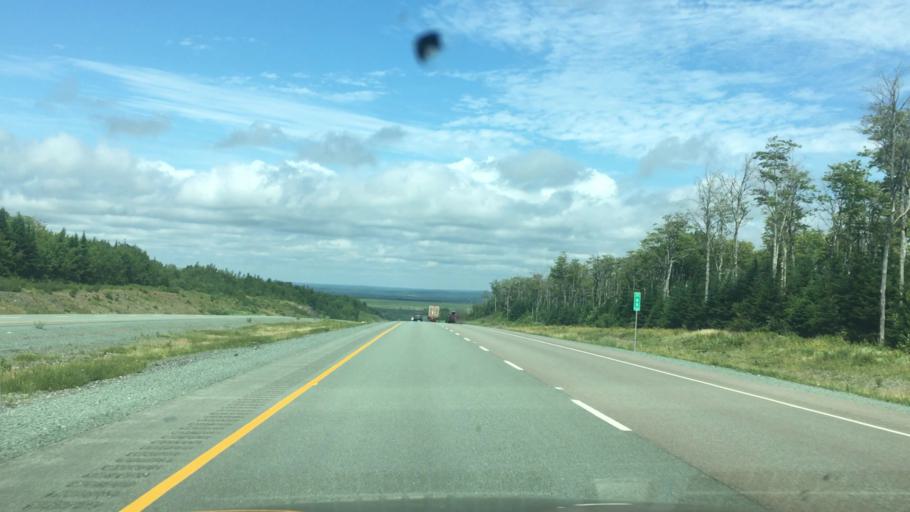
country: CA
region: Nova Scotia
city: Oxford
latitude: 45.5851
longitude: -63.7190
